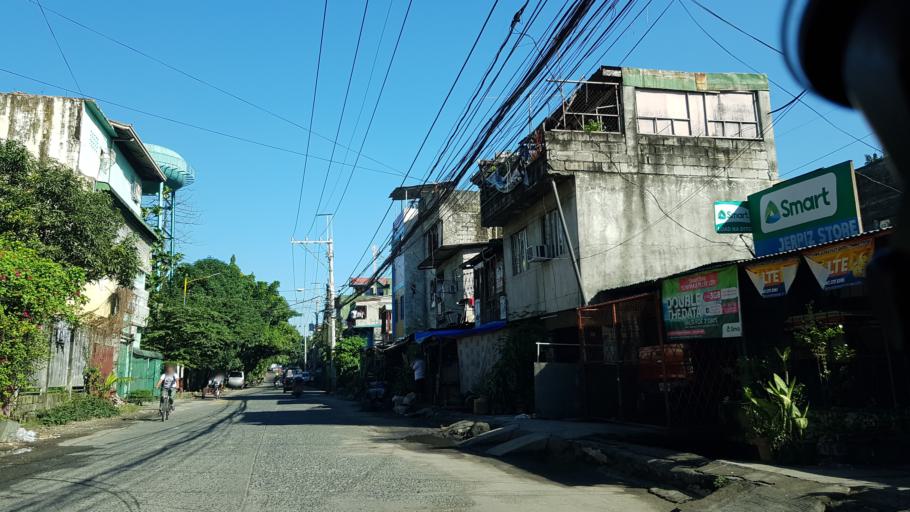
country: PH
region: Calabarzon
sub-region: Province of Rizal
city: Cainta
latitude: 14.5739
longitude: 121.0997
